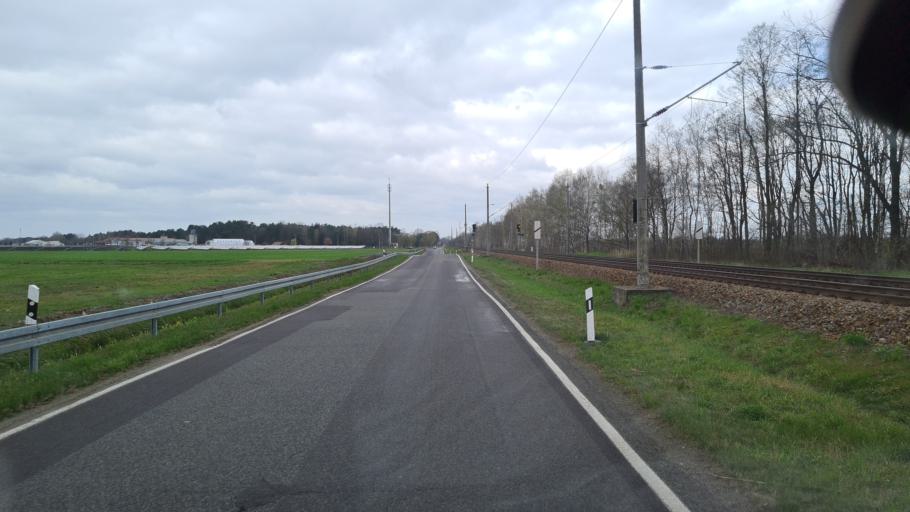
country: DE
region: Brandenburg
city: Ruhland
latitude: 51.4570
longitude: 13.8961
